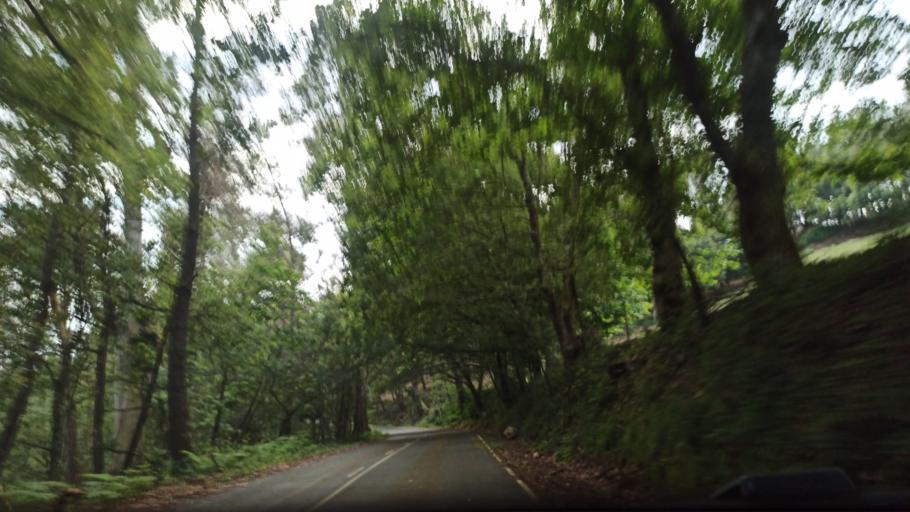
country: ES
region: Galicia
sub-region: Provincia da Coruna
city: Santiso
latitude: 42.8257
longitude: -8.1272
